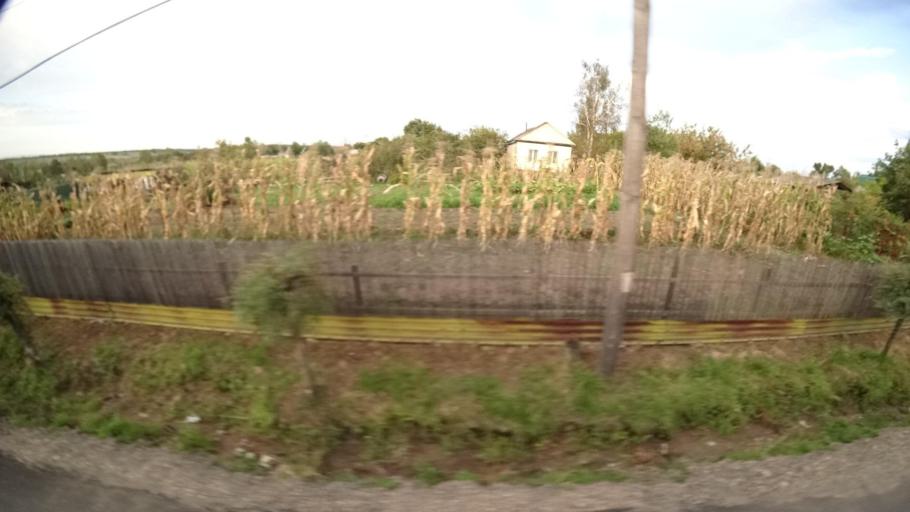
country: RU
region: Primorskiy
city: Yakovlevka
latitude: 44.4219
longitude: 133.4669
